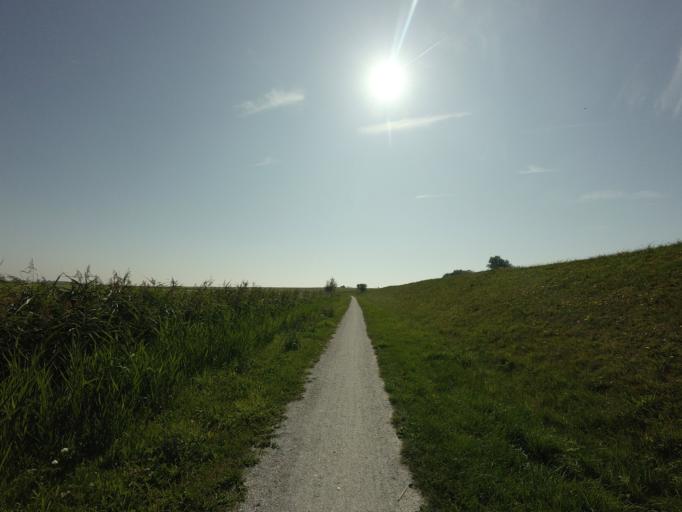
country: NL
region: Friesland
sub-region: Gemeente Schiermonnikoog
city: Schiermonnikoog
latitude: 53.4732
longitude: 6.1553
